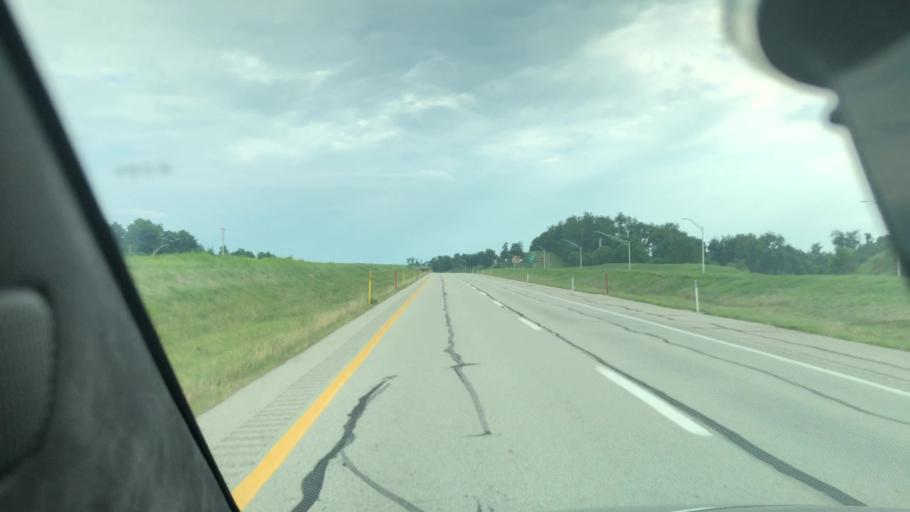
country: US
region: Pennsylvania
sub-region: Washington County
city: Baidland
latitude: 40.1951
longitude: -79.9882
